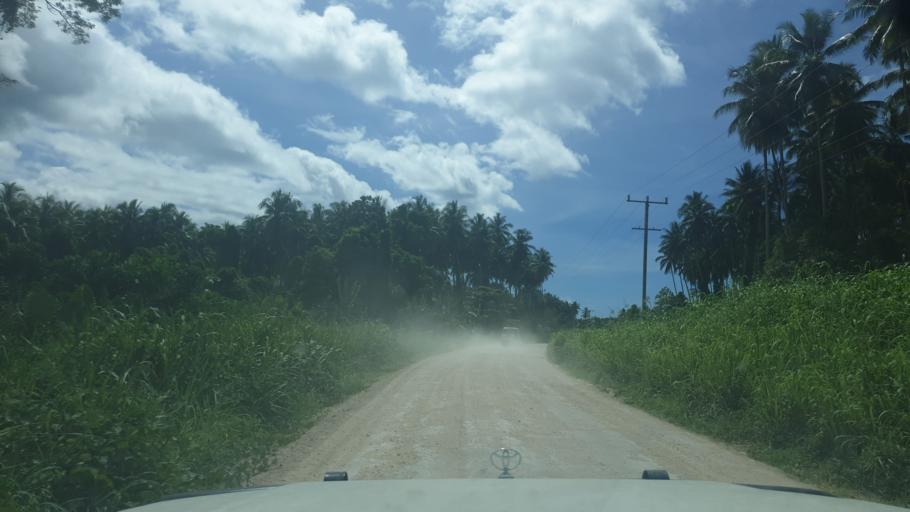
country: PG
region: Bougainville
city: Buka
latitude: -5.5024
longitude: 154.8091
